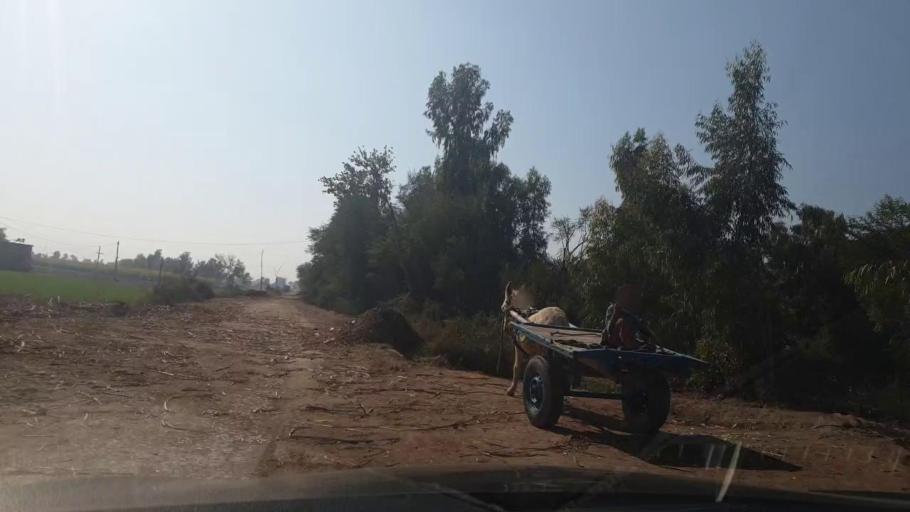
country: PK
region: Sindh
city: Ubauro
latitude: 28.1534
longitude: 69.6943
